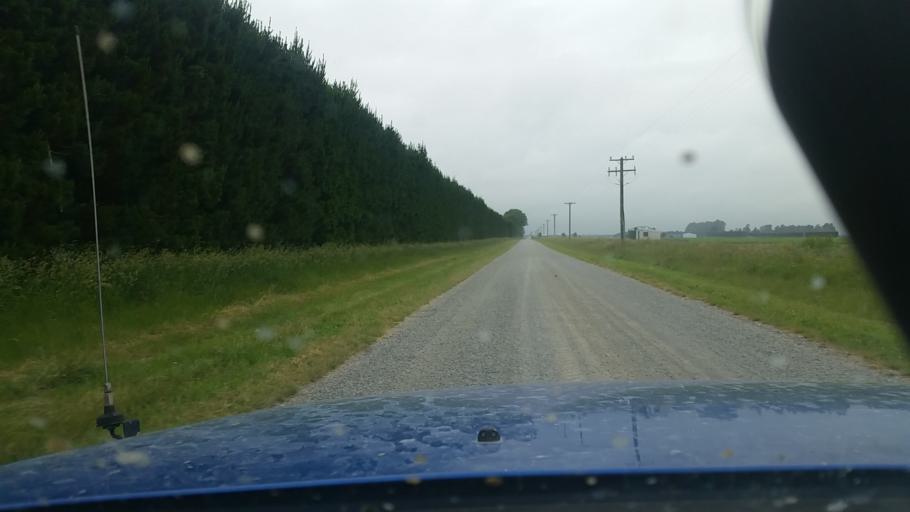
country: NZ
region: Canterbury
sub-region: Ashburton District
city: Rakaia
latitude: -43.8127
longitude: 171.8706
